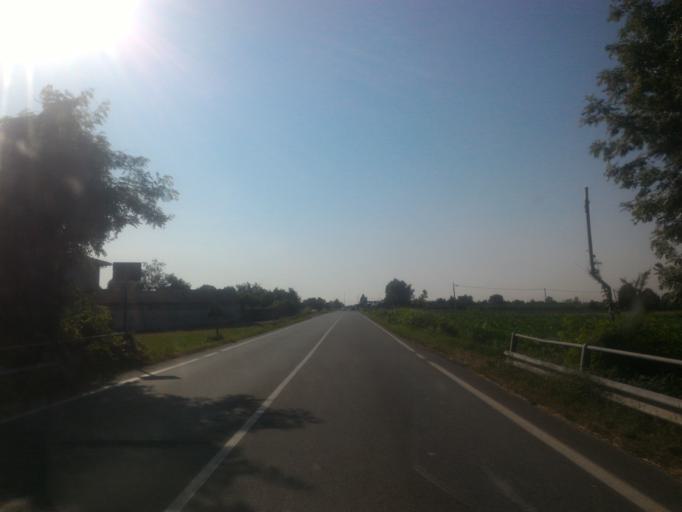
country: IT
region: Piedmont
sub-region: Provincia di Torino
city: Buriasco
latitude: 44.8734
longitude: 7.4040
